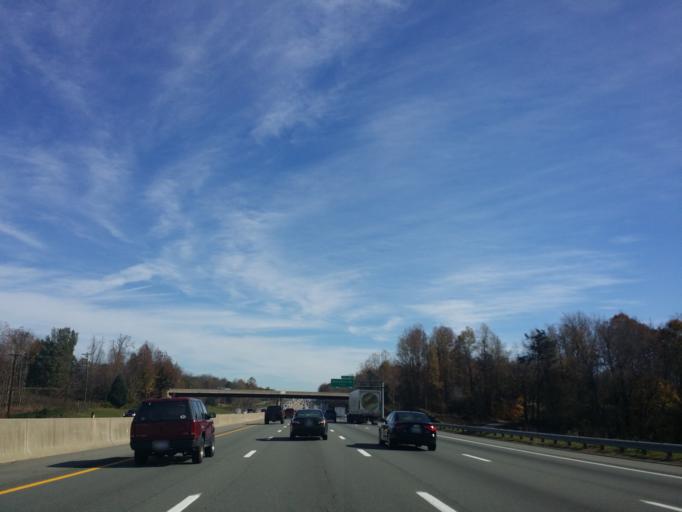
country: US
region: North Carolina
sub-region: Alamance County
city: Mebane
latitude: 36.0775
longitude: -79.2464
